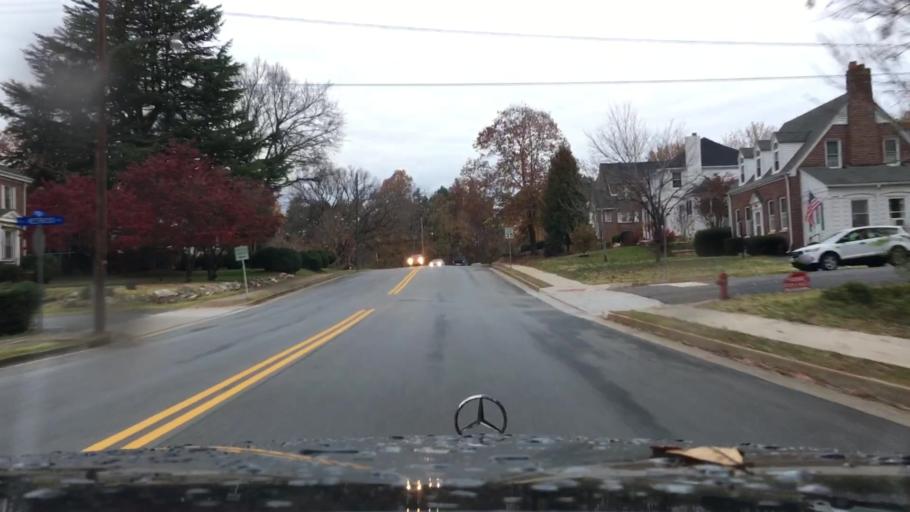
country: US
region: Virginia
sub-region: Campbell County
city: Altavista
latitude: 37.1154
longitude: -79.3001
